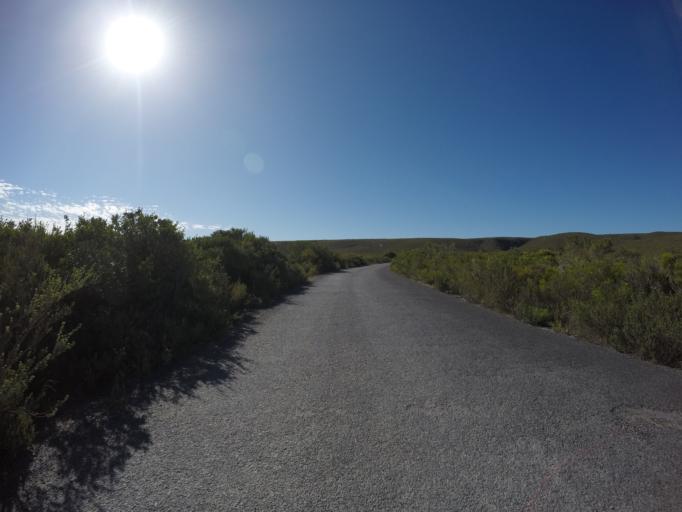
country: ZA
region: Western Cape
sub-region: Overberg District Municipality
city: Bredasdorp
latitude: -34.4336
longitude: 20.4188
